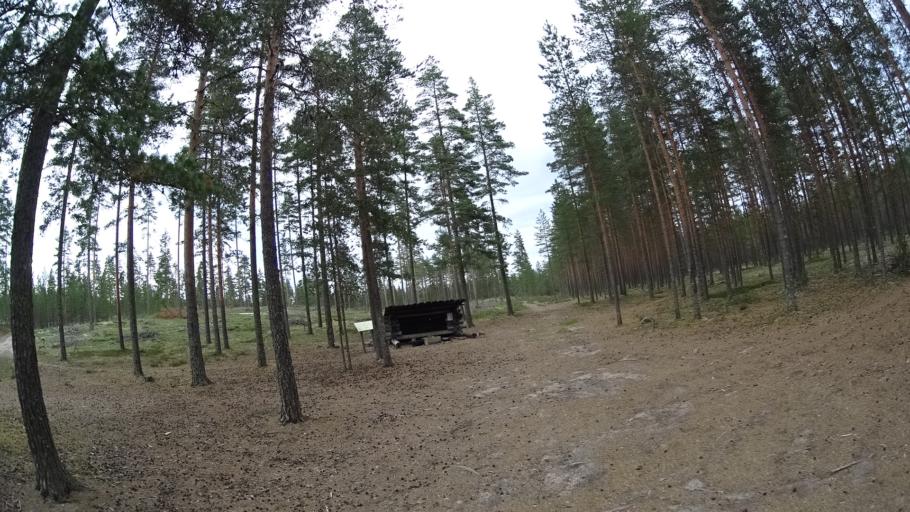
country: FI
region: Satakunta
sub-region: Pohjois-Satakunta
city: Jaemijaervi
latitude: 61.7597
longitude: 22.7813
